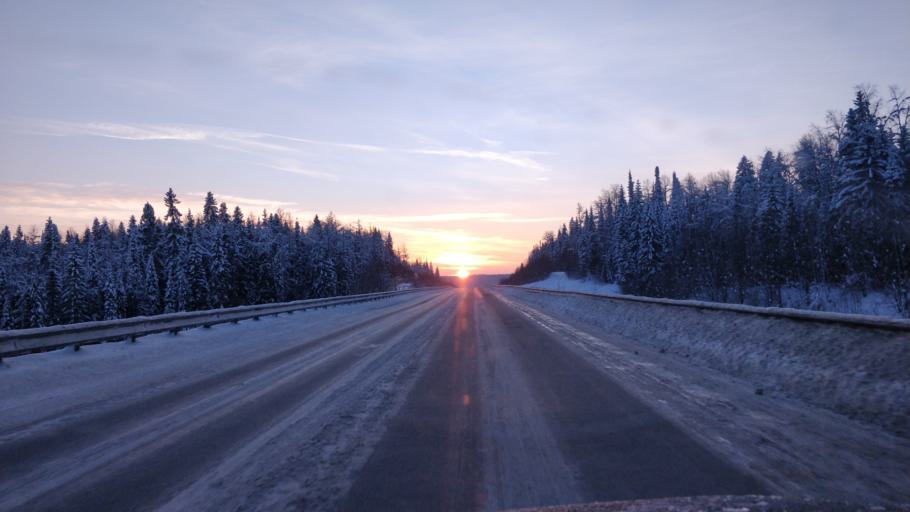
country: RU
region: Perm
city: Sylva
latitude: 58.2908
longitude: 56.7485
